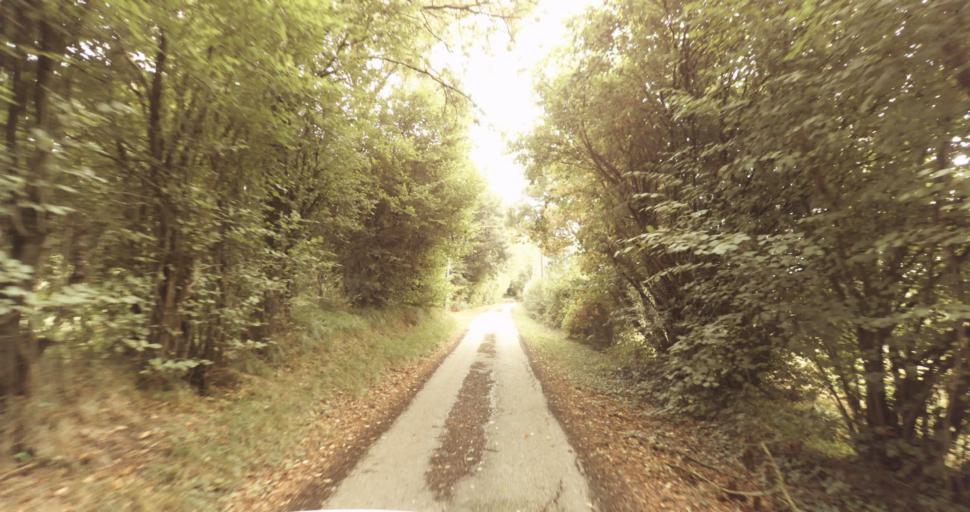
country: FR
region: Lower Normandy
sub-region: Departement du Calvados
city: Livarot
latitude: 48.9374
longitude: 0.0870
